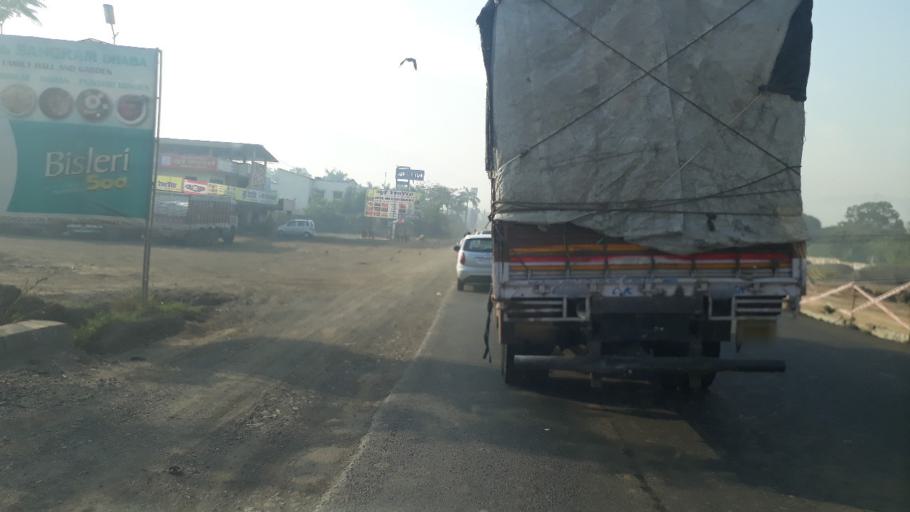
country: IN
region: Maharashtra
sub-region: Raigarh
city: Kalundri
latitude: 18.9293
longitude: 73.1273
